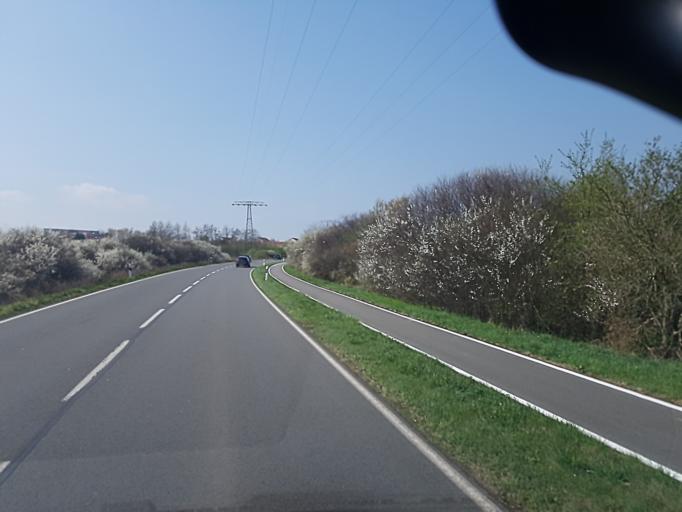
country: DE
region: Saxony-Anhalt
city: Grafenhainichen
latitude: 51.7373
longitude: 12.4618
